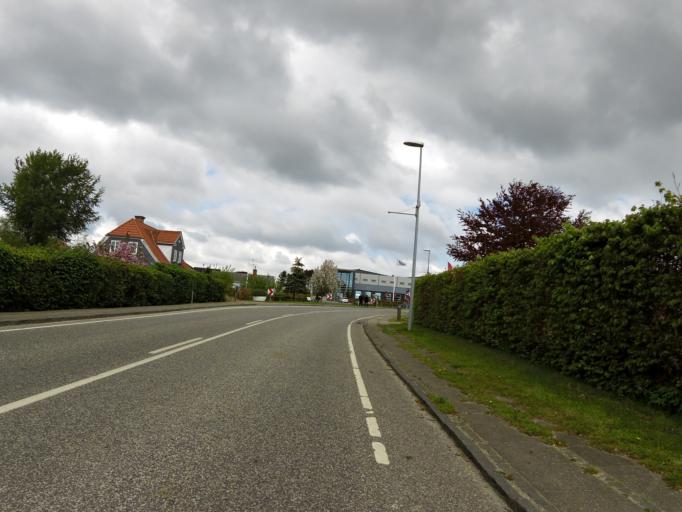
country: DK
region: South Denmark
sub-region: Haderslev Kommune
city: Gram
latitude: 55.2734
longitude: 9.0059
